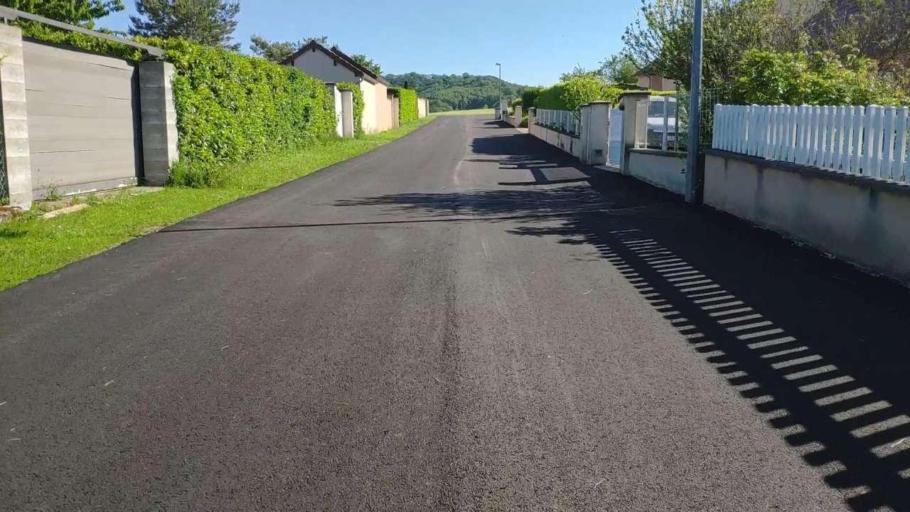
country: FR
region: Franche-Comte
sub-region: Departement du Jura
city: Montmorot
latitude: 46.7351
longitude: 5.5534
